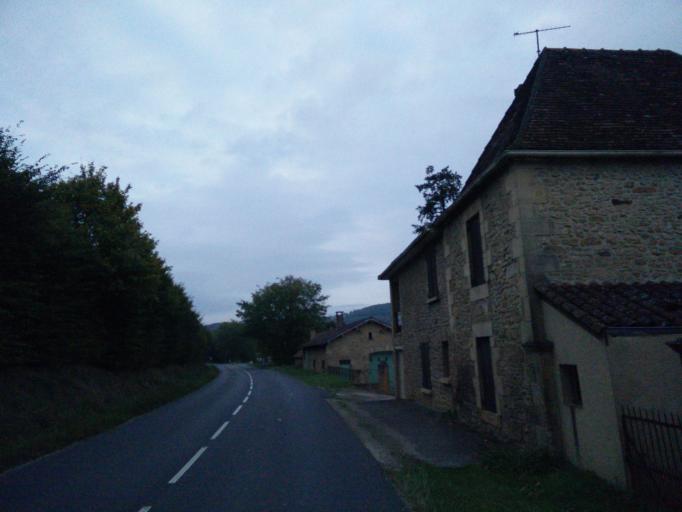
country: FR
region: Aquitaine
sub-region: Departement de la Dordogne
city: Carsac-Aillac
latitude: 44.8336
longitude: 1.2749
